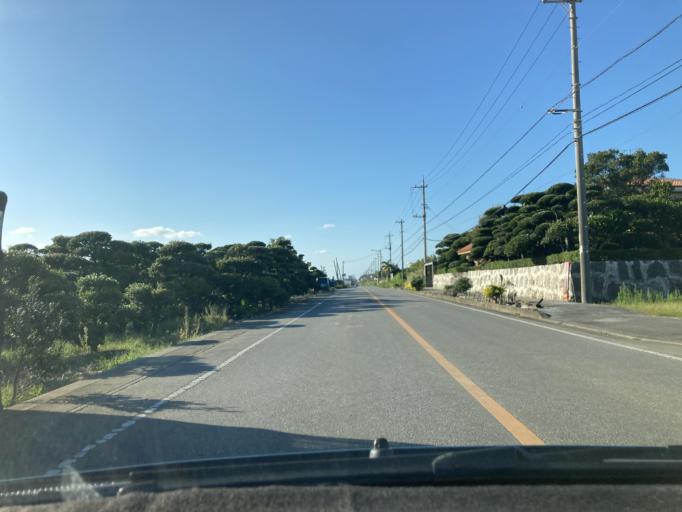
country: JP
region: Okinawa
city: Itoman
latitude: 26.0999
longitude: 127.6748
